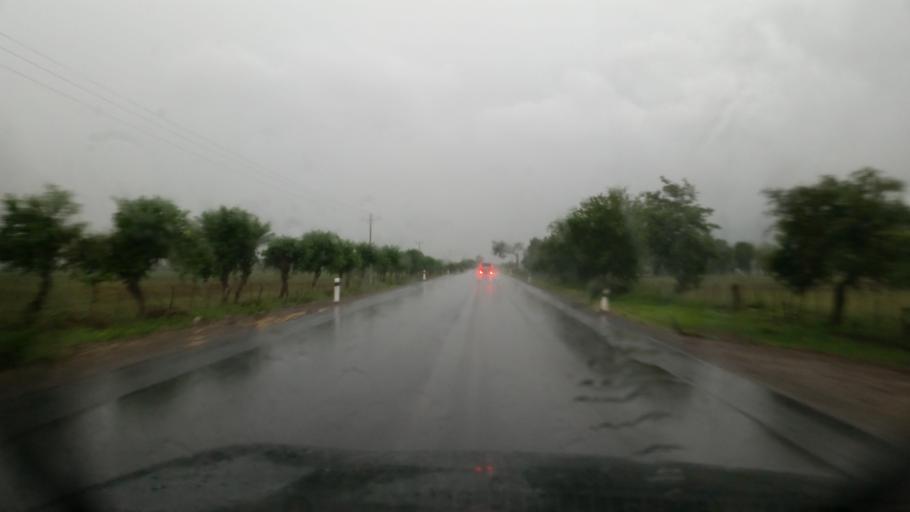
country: NI
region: Chinandega
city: Chichigalpa
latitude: 12.7755
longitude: -86.9223
